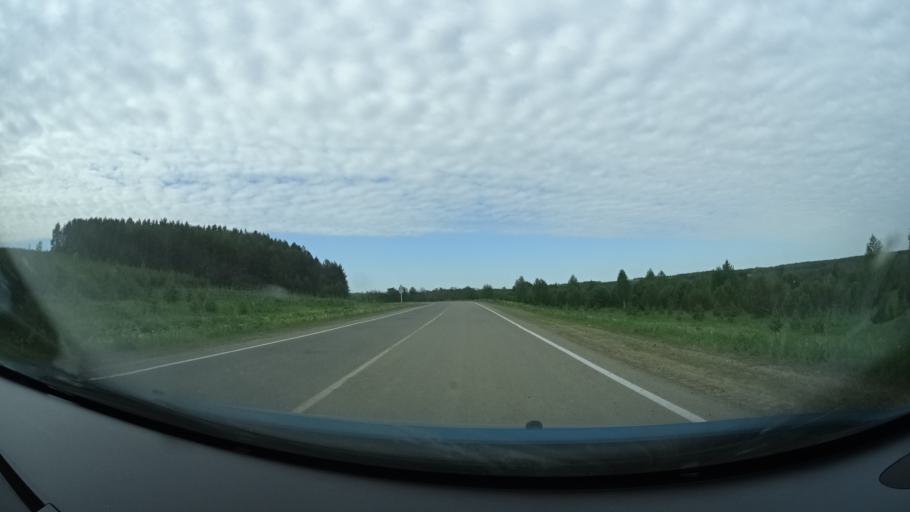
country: RU
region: Perm
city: Kuyeda
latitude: 56.5236
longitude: 55.6278
